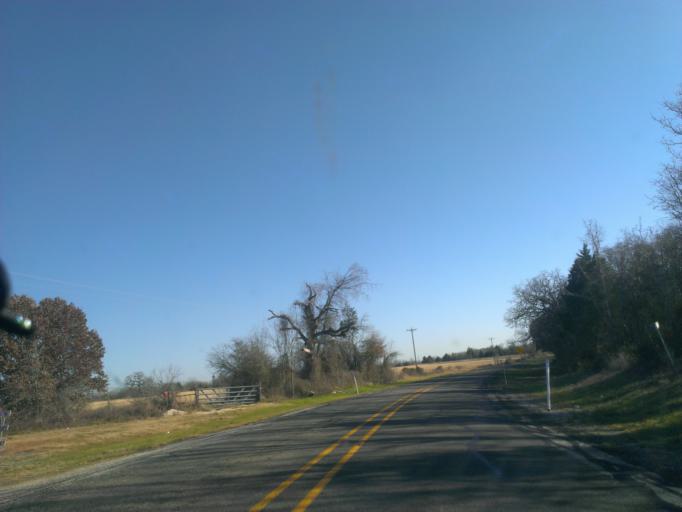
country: US
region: Texas
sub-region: Bastrop County
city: Elgin
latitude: 30.4414
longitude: -97.2608
